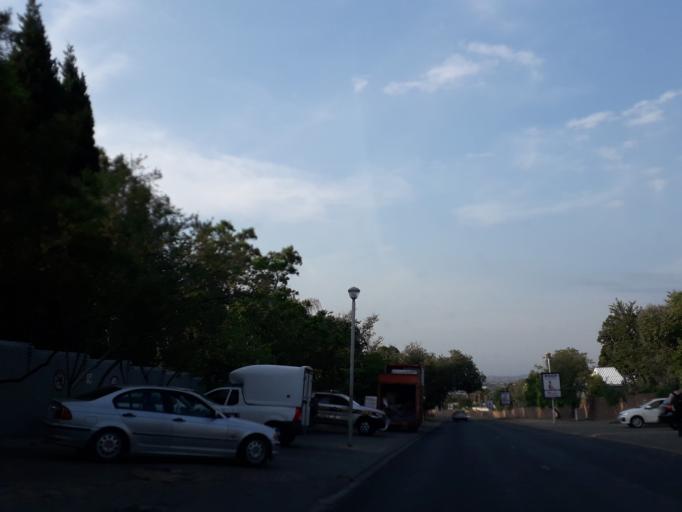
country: ZA
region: Gauteng
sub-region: City of Johannesburg Metropolitan Municipality
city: Diepsloot
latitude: -26.0054
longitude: 28.0021
